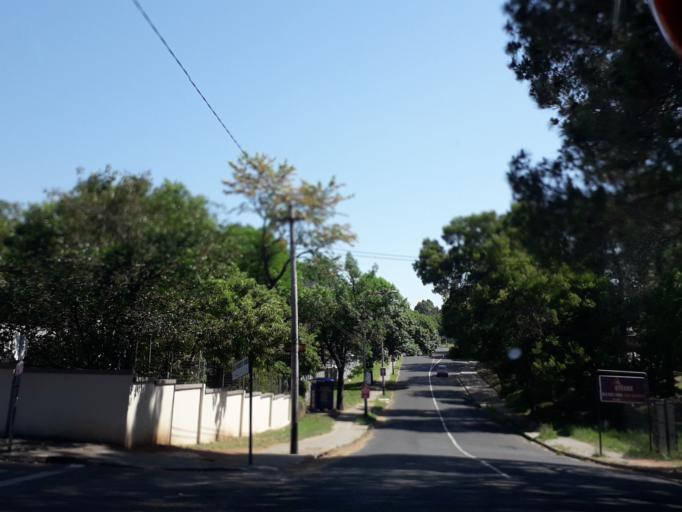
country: ZA
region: Gauteng
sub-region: City of Johannesburg Metropolitan Municipality
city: Johannesburg
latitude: -26.1484
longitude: 28.0775
